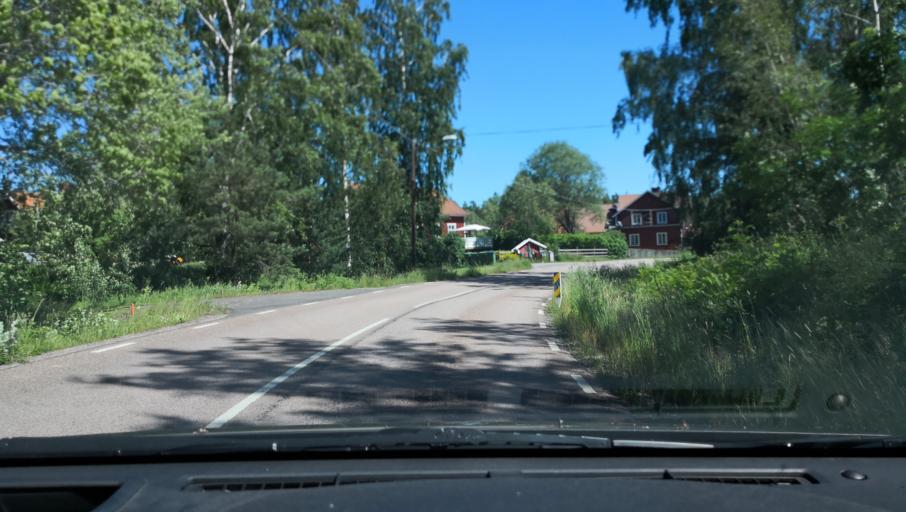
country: SE
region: Vaestmanland
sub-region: Arboga Kommun
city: Tyringe
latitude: 59.2947
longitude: 16.0432
